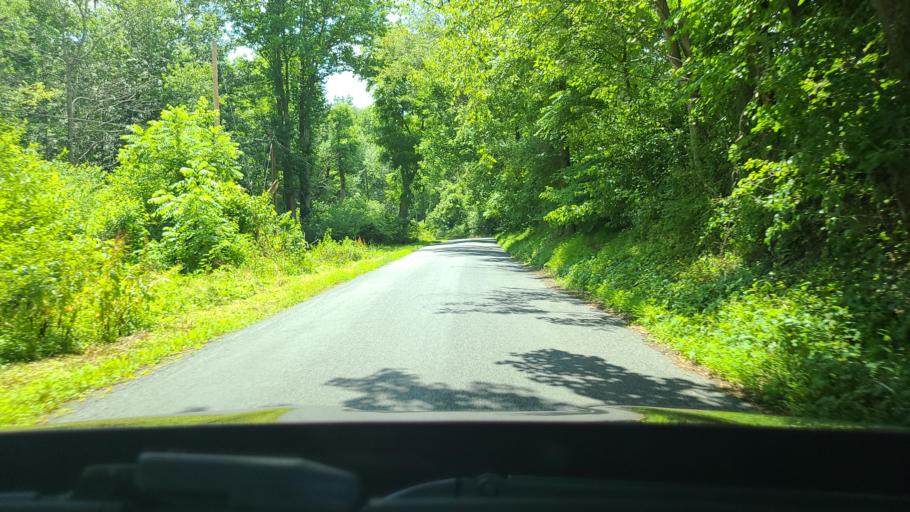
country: US
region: Maryland
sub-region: Montgomery County
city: Damascus
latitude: 39.2690
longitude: -77.2391
